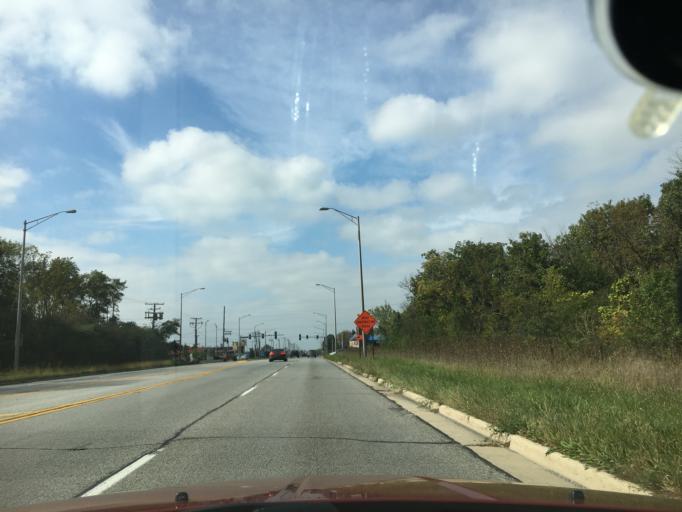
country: US
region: Illinois
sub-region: Cook County
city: Tinley Park
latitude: 41.6025
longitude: -87.7829
